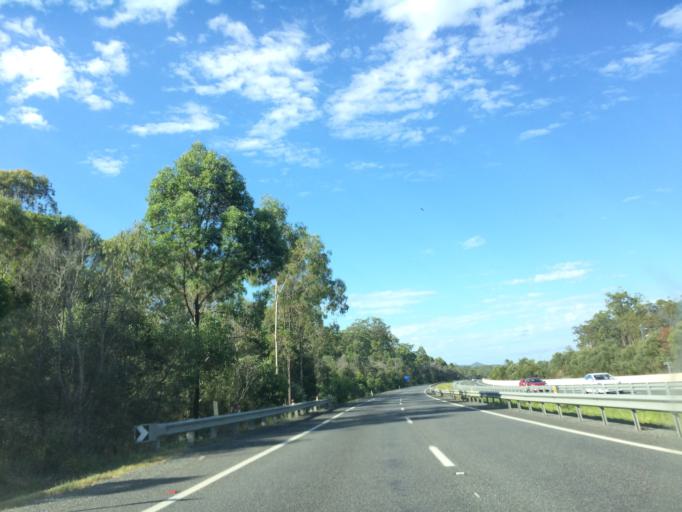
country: AU
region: Queensland
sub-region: Ipswich
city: Springfield
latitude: -27.6426
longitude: 152.9378
